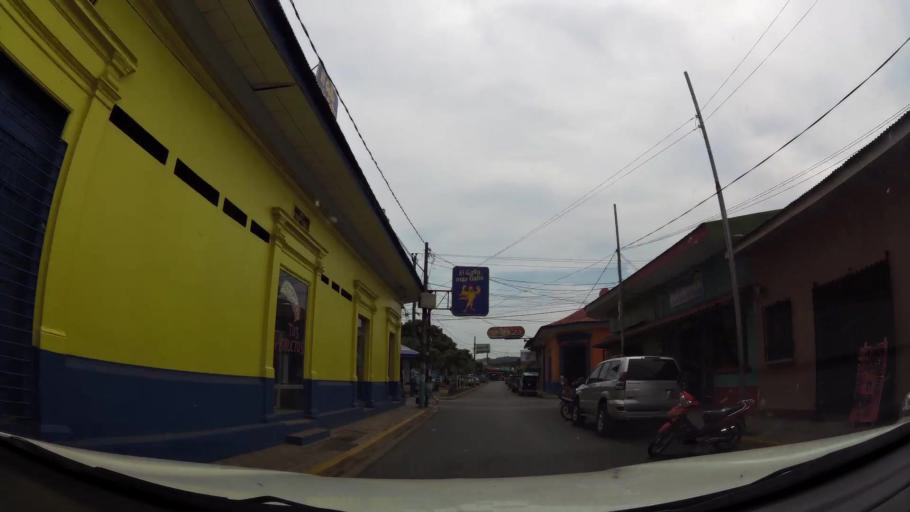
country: NI
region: Rivas
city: Rivas
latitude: 11.4394
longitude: -85.8306
